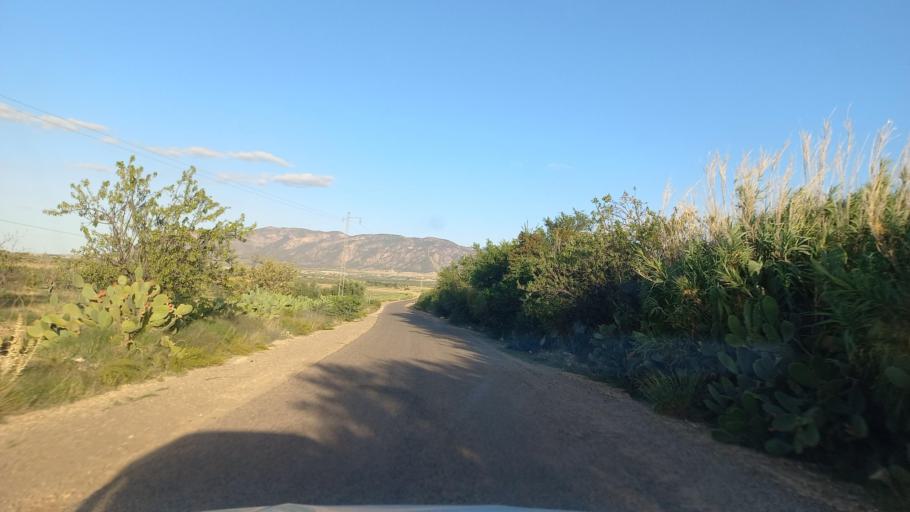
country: TN
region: Al Qasrayn
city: Sbiba
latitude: 35.4113
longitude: 9.1338
